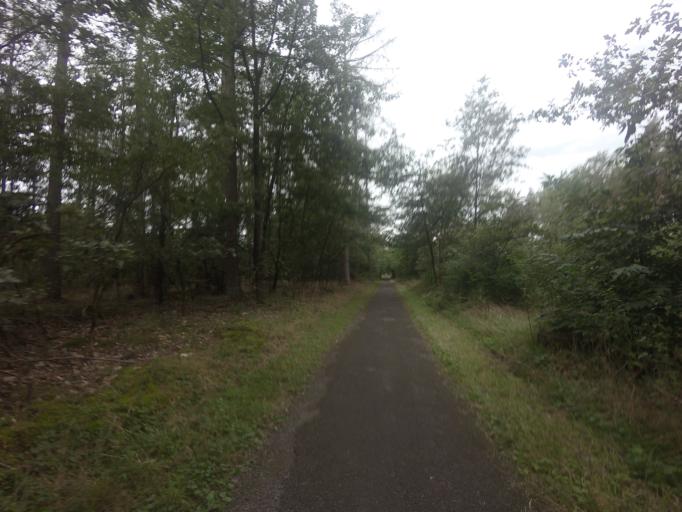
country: NL
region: Drenthe
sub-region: Gemeente Westerveld
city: Dwingeloo
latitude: 52.9082
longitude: 6.3112
